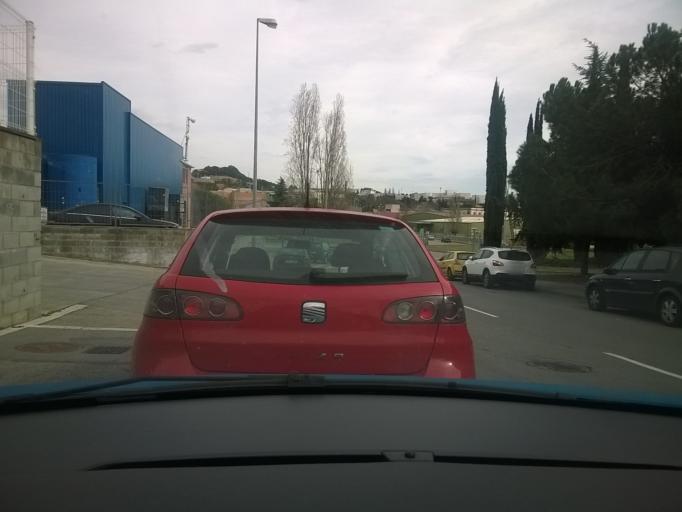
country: ES
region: Catalonia
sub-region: Provincia de Barcelona
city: Rubi
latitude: 41.5083
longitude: 2.0320
